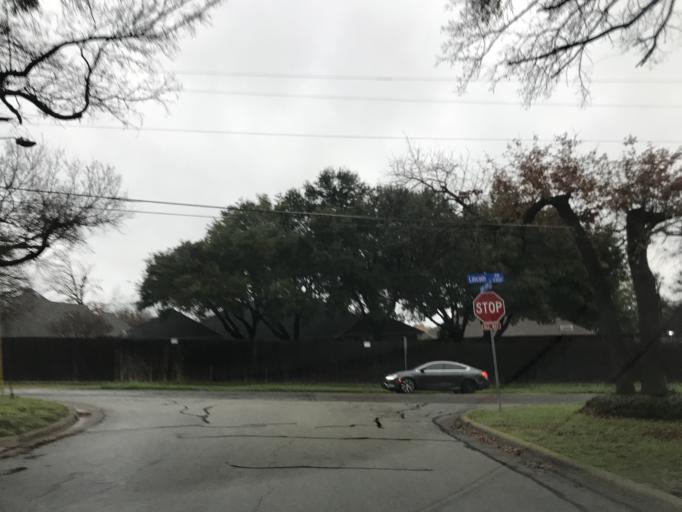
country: US
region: Texas
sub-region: Tarrant County
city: Arlington
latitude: 32.7723
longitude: -97.1054
